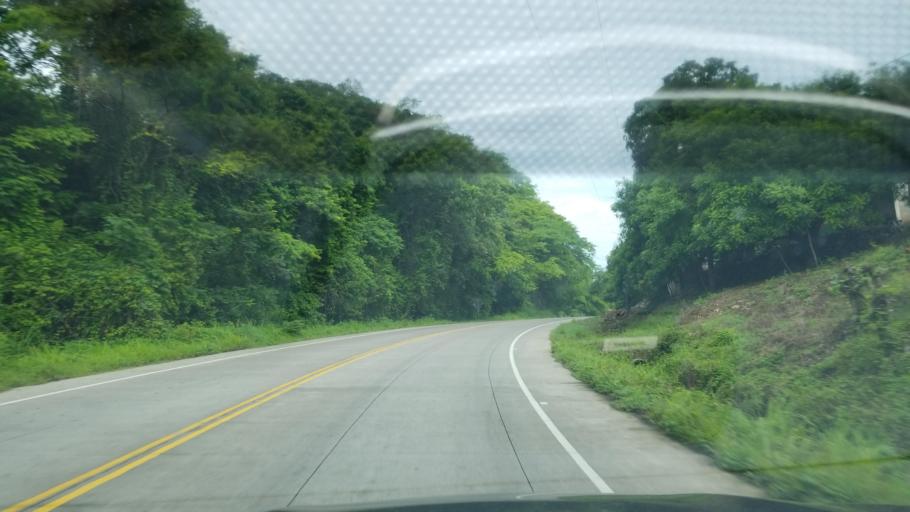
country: HN
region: Francisco Morazan
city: El Porvenir
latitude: 13.6858
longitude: -87.3357
